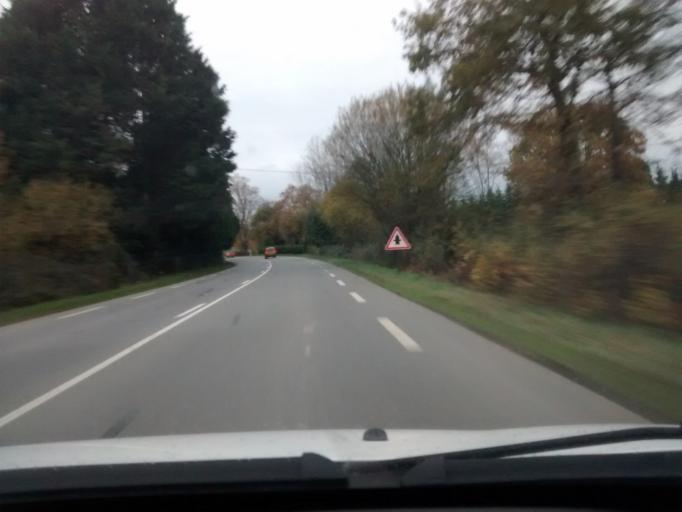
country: FR
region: Brittany
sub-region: Departement d'Ille-et-Vilaine
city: Fouillard
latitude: 48.1408
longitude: -1.5671
